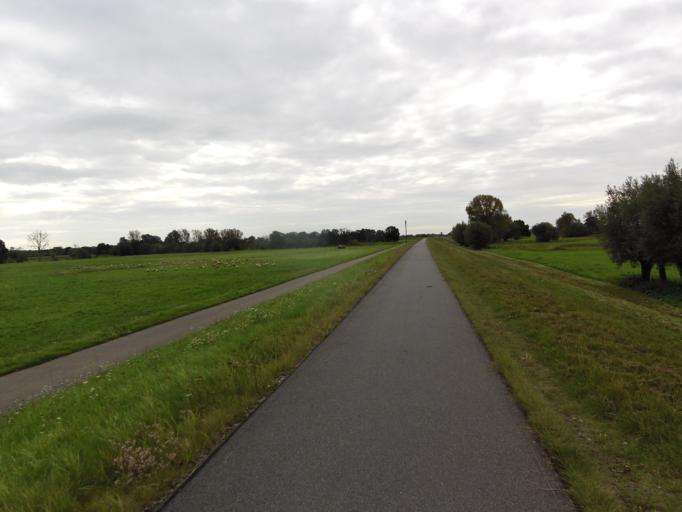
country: DE
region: Brandenburg
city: Breese
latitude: 52.9704
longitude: 11.7868
